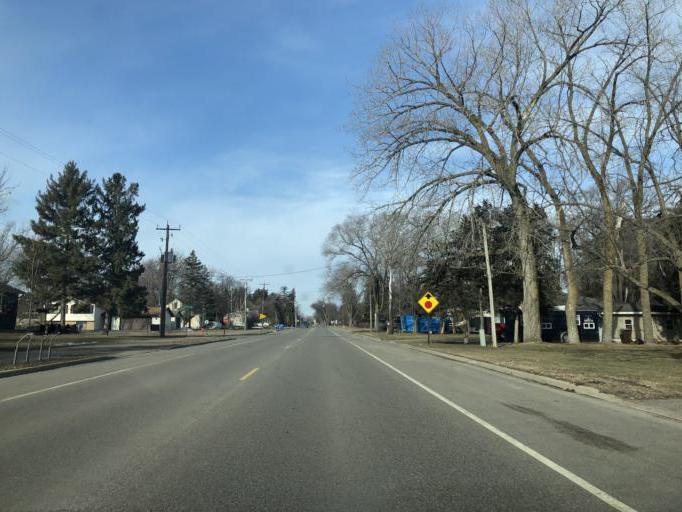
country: US
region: Minnesota
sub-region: Sherburne County
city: Becker
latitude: 45.3937
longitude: -93.8670
